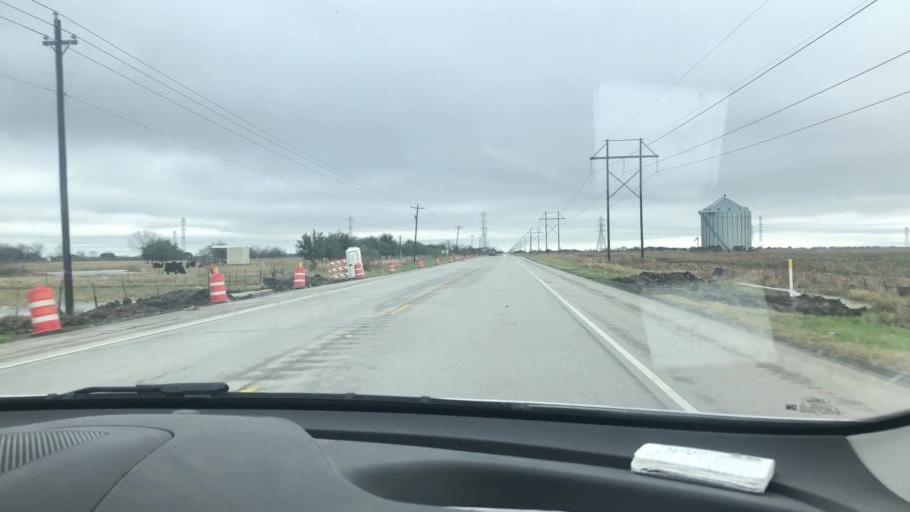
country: US
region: Texas
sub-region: Wharton County
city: Boling
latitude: 29.1795
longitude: -96.0076
